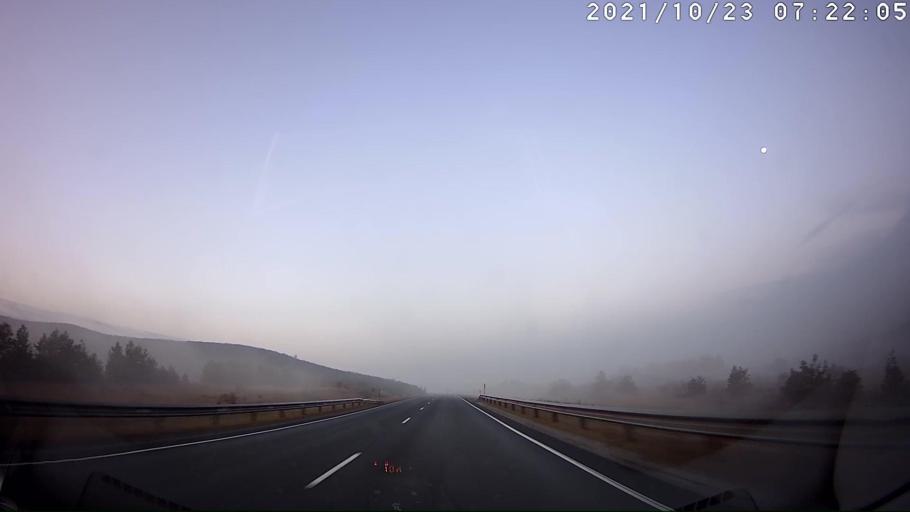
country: RU
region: Saratov
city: Alekseyevka
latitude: 52.3998
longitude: 47.9888
